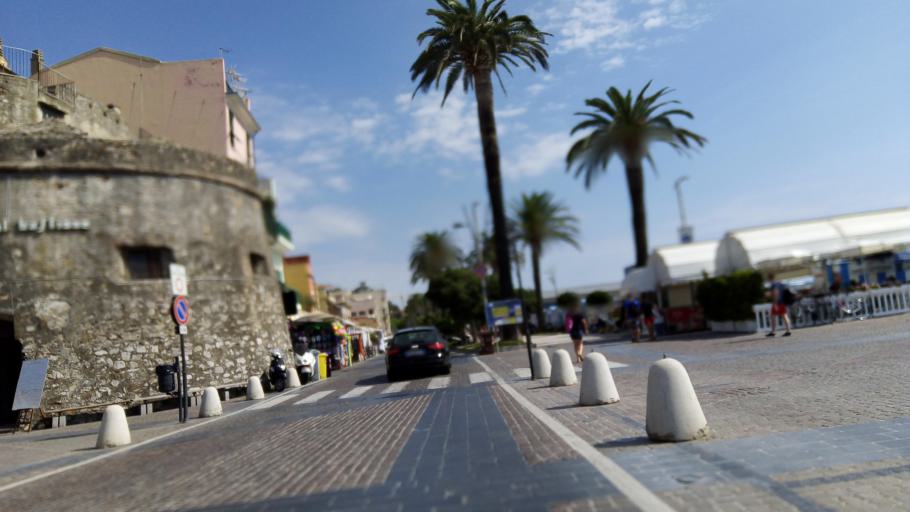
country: IT
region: Liguria
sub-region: Provincia di Savona
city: Ceriale
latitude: 44.0963
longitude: 8.2335
